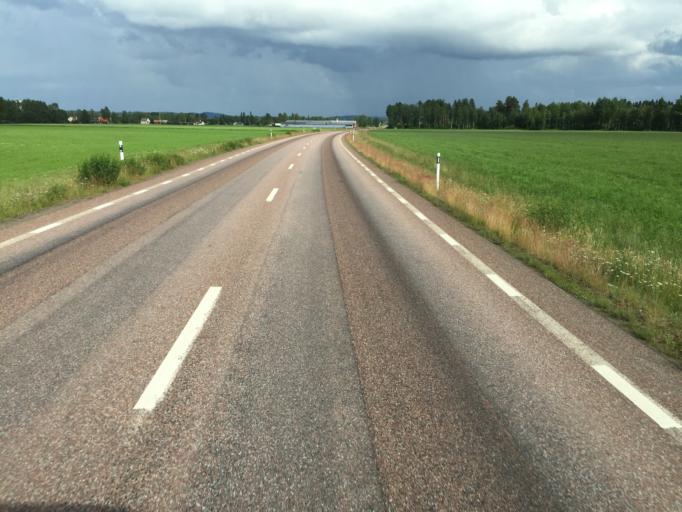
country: SE
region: Dalarna
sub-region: Vansbro Kommun
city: Jarna
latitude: 60.5542
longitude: 14.3410
